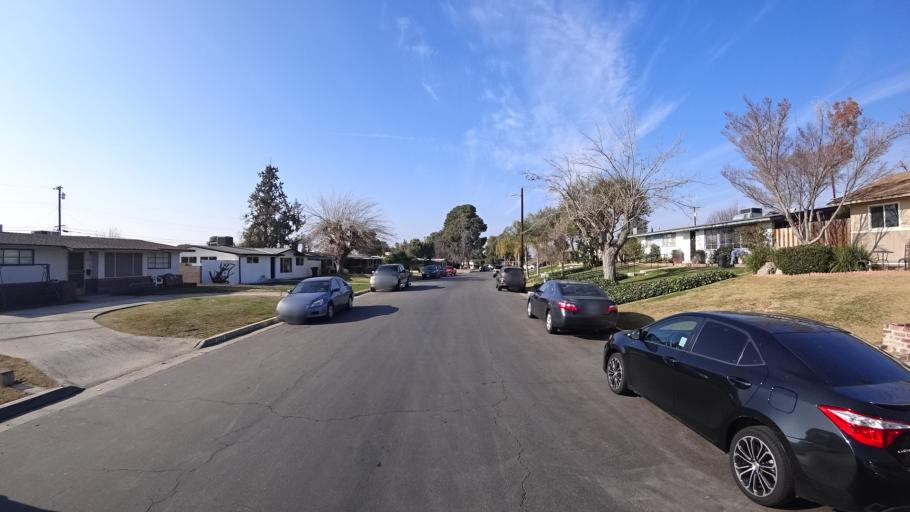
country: US
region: California
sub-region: Kern County
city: Oildale
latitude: 35.4057
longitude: -118.9830
